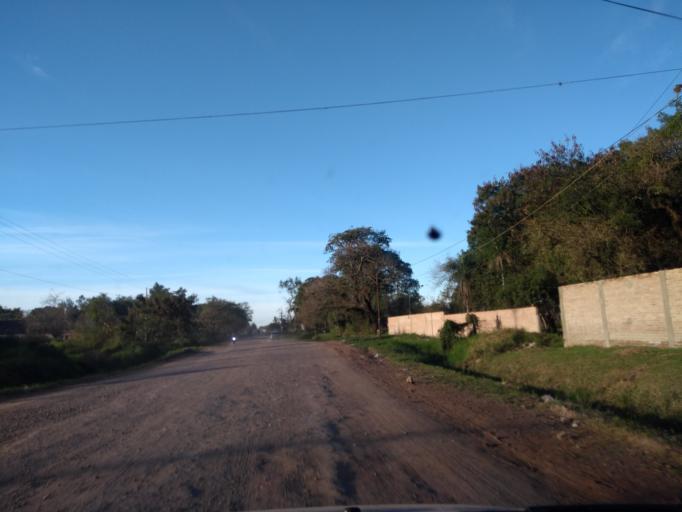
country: AR
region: Chaco
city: Resistencia
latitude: -27.4906
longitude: -58.9733
